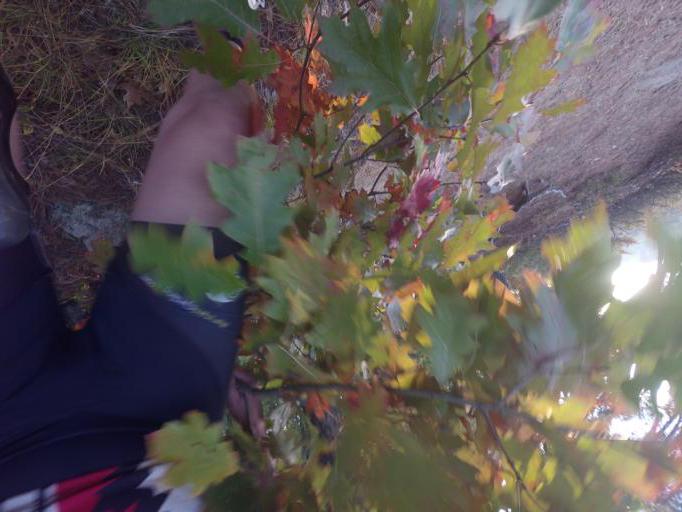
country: CA
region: Ontario
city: Deep River
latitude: 45.8854
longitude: -77.6354
